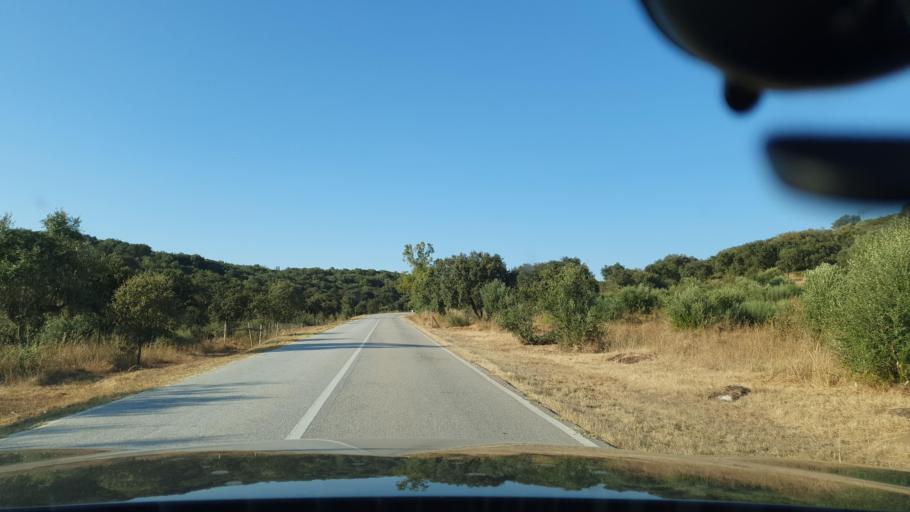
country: PT
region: Evora
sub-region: Estremoz
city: Estremoz
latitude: 38.9045
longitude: -7.6676
